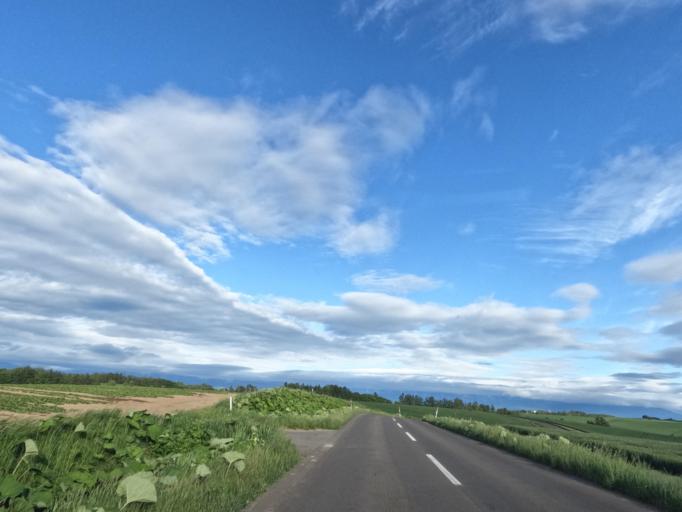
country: JP
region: Hokkaido
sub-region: Asahikawa-shi
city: Asahikawa
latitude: 43.6259
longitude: 142.4371
